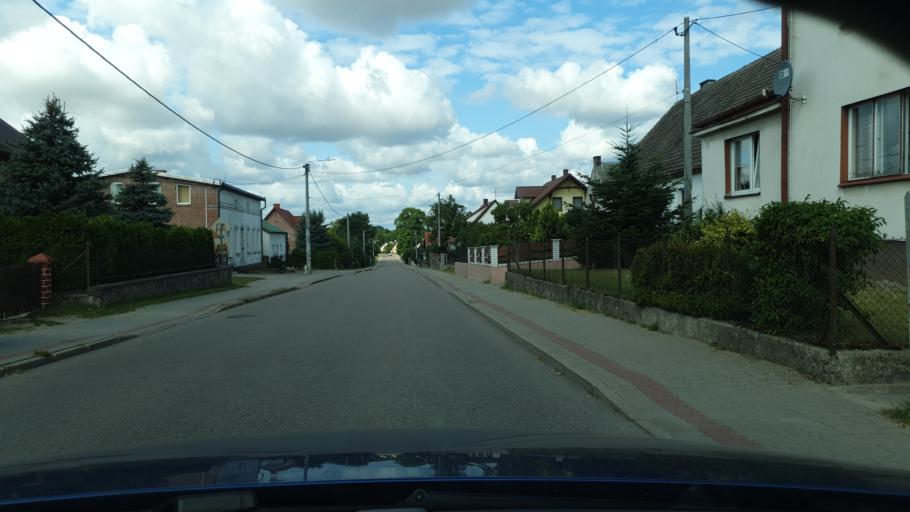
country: PL
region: Pomeranian Voivodeship
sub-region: Powiat czluchowski
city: Przechlewo
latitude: 53.8065
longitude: 17.3407
